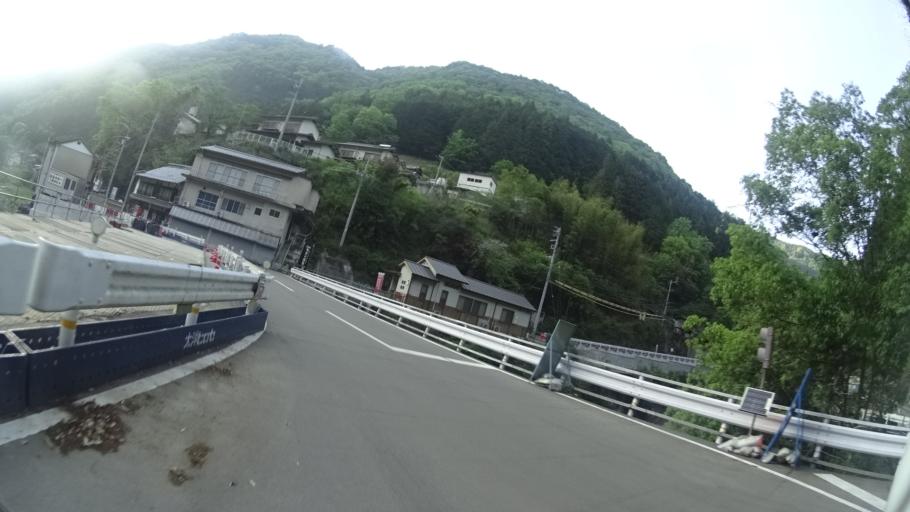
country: JP
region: Tokushima
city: Ikedacho
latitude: 33.9575
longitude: 133.7999
